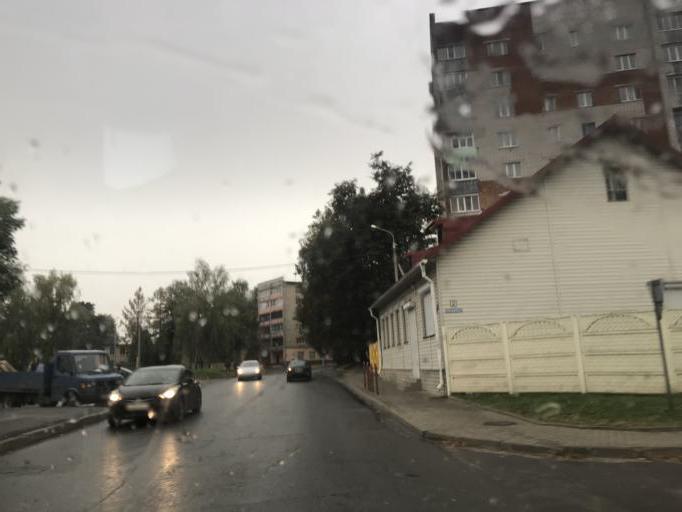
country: BY
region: Mogilev
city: Mahilyow
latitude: 53.8942
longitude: 30.3183
